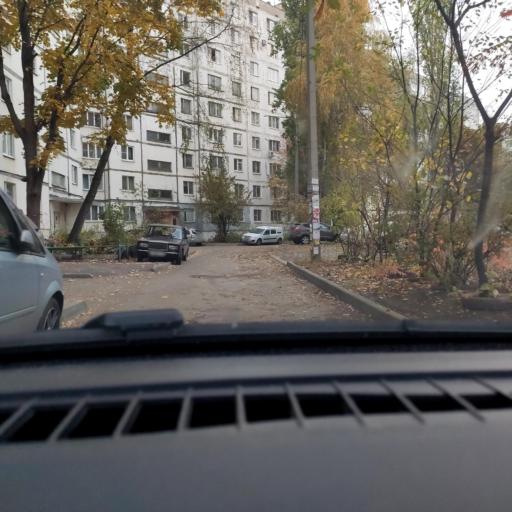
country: RU
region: Voronezj
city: Podgornoye
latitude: 51.7036
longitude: 39.1546
